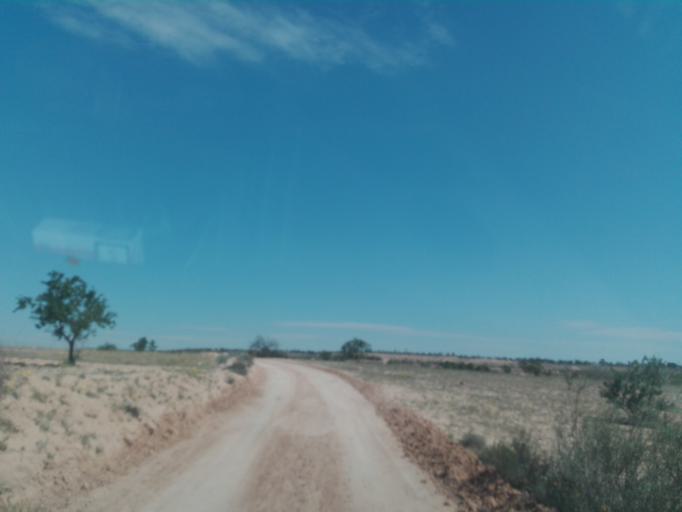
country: TN
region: Safaqis
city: Sfax
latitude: 34.6919
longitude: 10.5303
